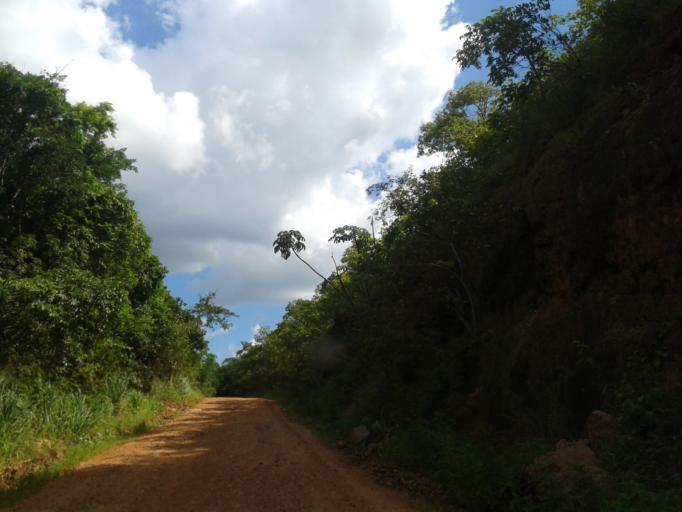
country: BR
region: Minas Gerais
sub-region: Campina Verde
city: Campina Verde
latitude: -19.3235
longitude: -49.8014
